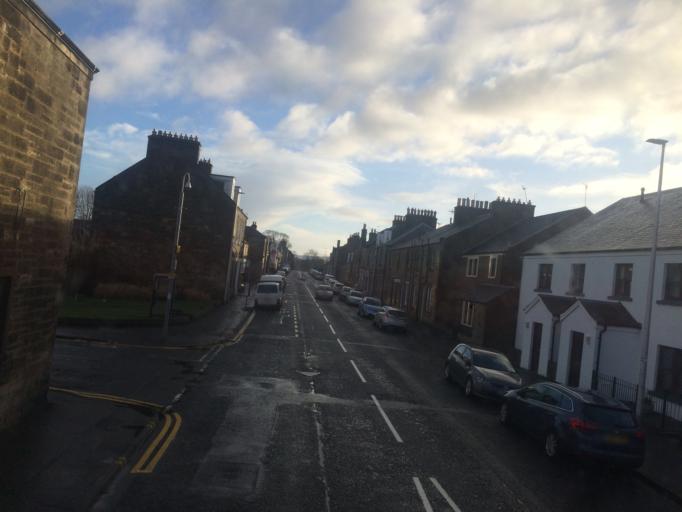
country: GB
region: Scotland
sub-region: Midlothian
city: Loanhead
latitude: 55.8584
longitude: -3.1662
